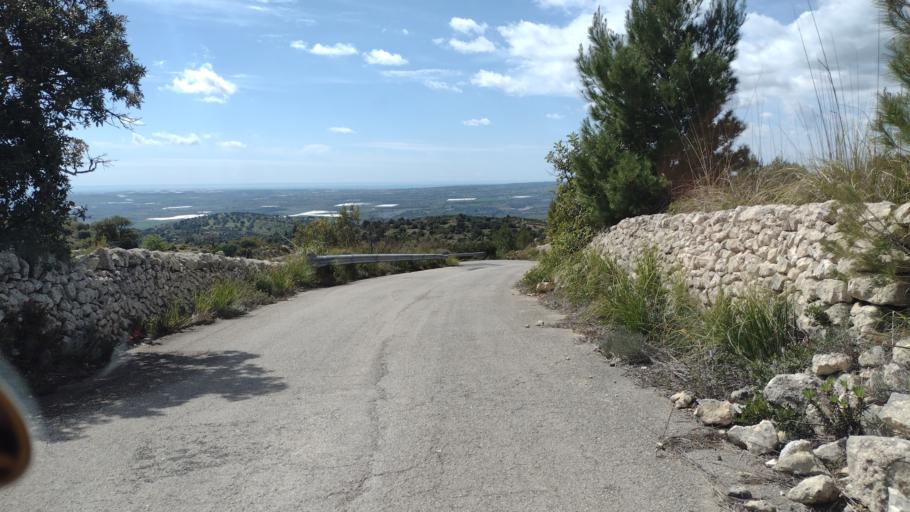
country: IT
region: Sicily
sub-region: Provincia di Siracusa
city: Noto
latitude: 36.9127
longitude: 14.9795
